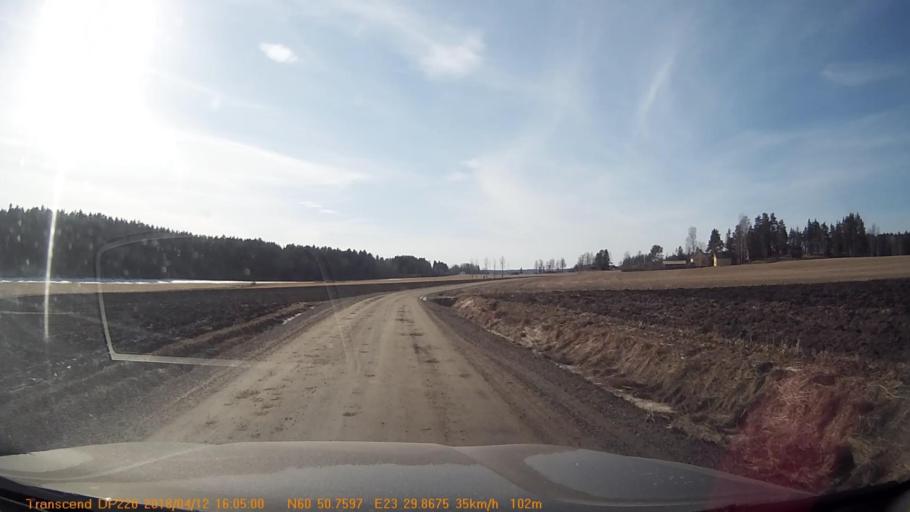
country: FI
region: Haeme
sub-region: Forssa
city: Jokioinen
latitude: 60.8460
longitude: 23.4976
